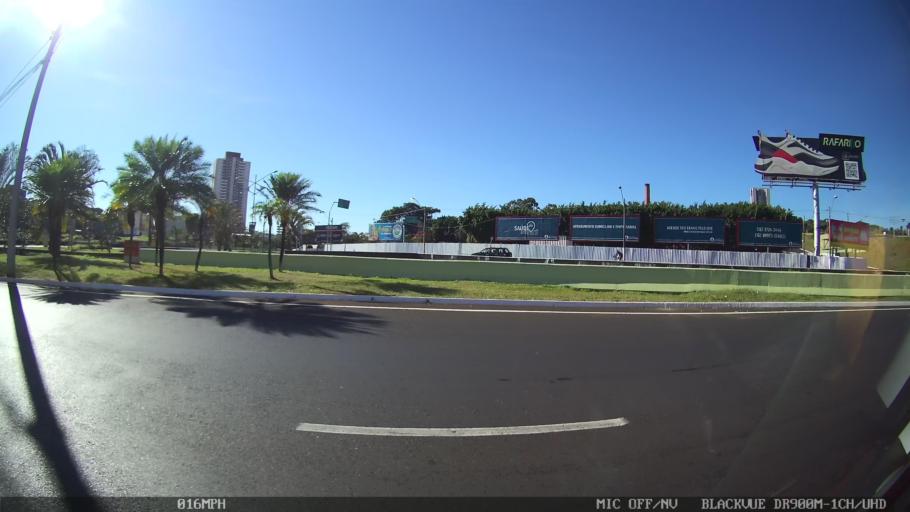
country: BR
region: Sao Paulo
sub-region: Franca
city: Franca
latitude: -20.5524
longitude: -47.4102
